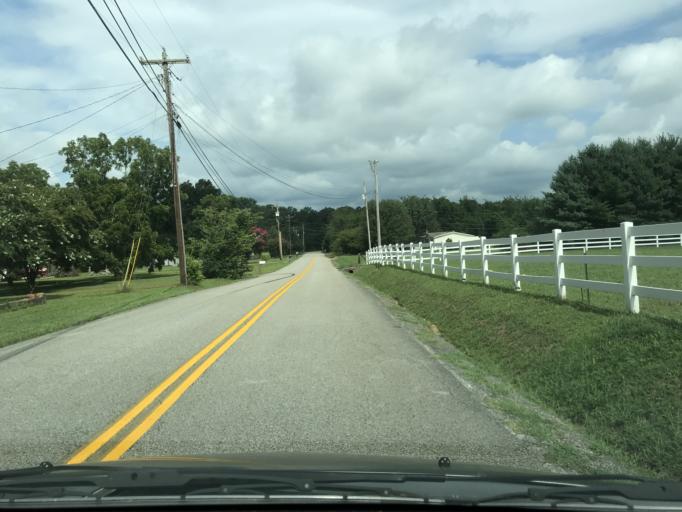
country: US
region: Tennessee
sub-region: Hamilton County
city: Lakesite
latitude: 35.1880
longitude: -85.1058
